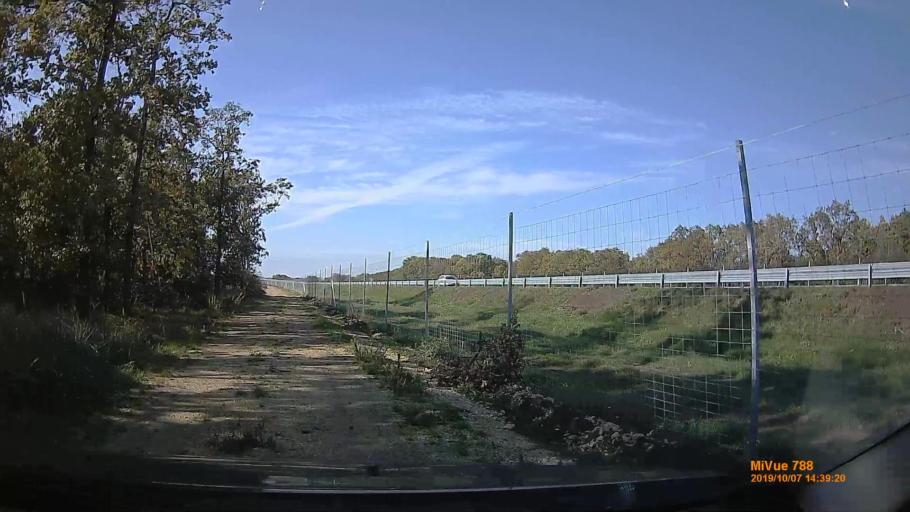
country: HU
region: Jasz-Nagykun-Szolnok
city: Kunszentmarton
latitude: 46.8567
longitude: 20.3096
